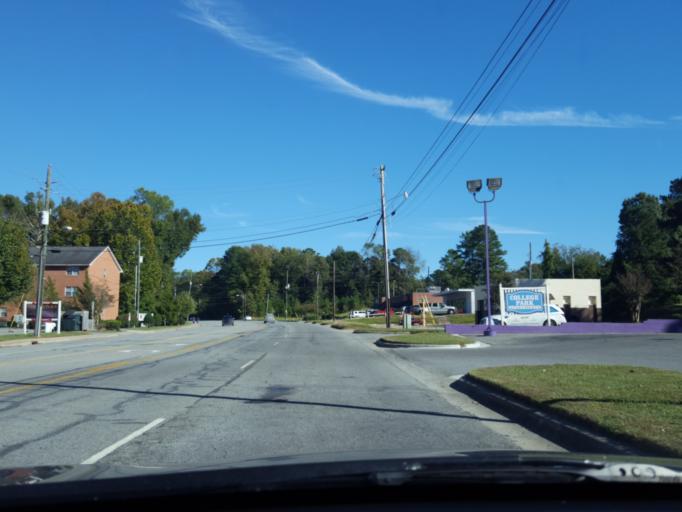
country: US
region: North Carolina
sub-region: Pitt County
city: Greenville
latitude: 35.6026
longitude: -77.3530
